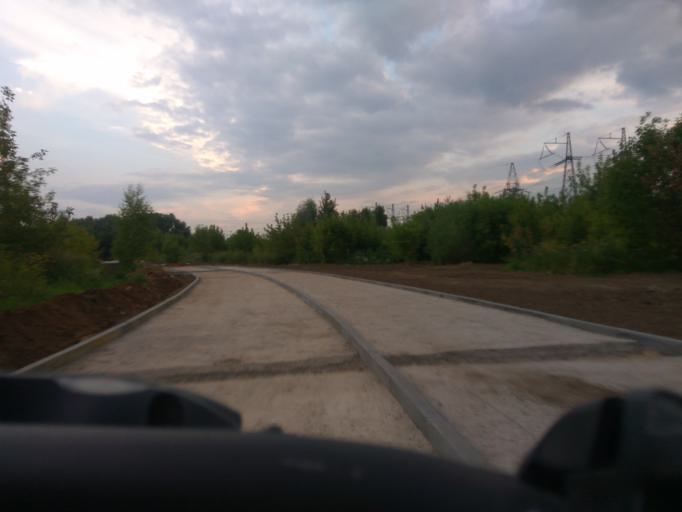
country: RU
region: Moscow
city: Brateyevo
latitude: 55.6418
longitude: 37.7767
